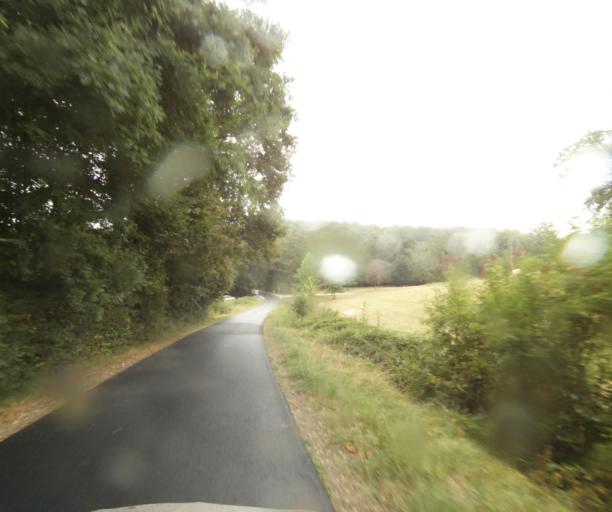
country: FR
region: Aquitaine
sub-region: Departement de la Gironde
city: Creon
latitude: 44.7576
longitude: -0.3517
